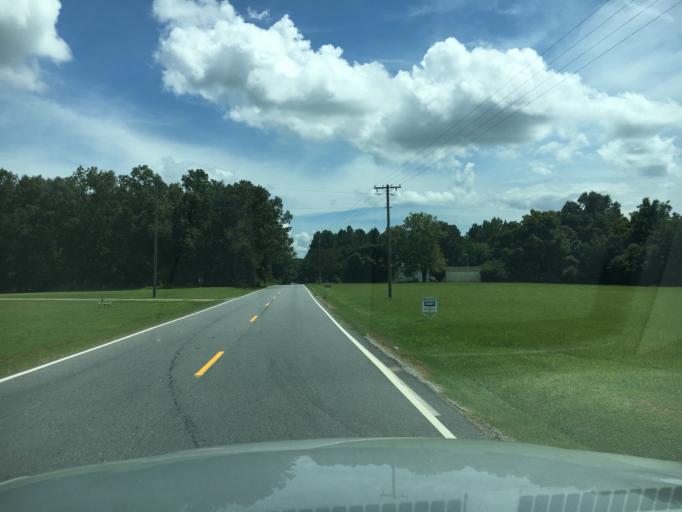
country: US
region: South Carolina
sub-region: Anderson County
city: Belton
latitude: 34.5308
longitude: -82.4333
